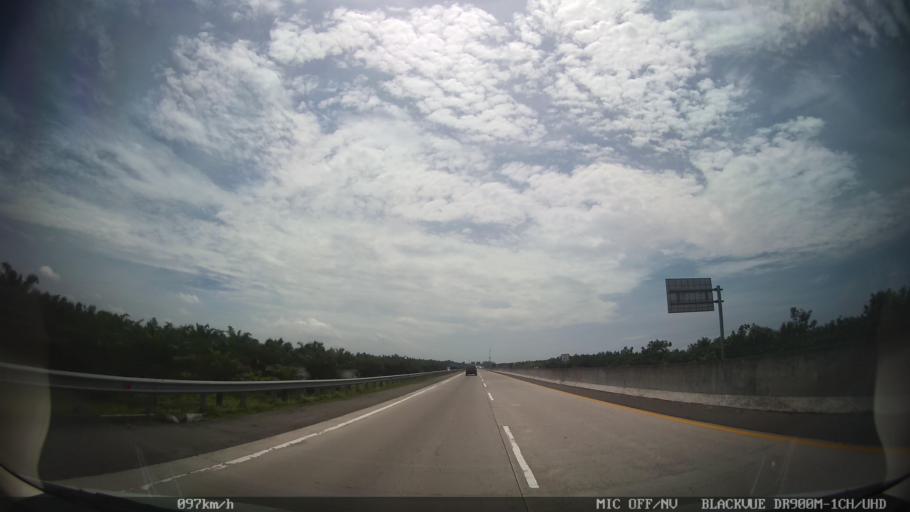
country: ID
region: North Sumatra
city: Percut
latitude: 3.5351
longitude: 98.8627
